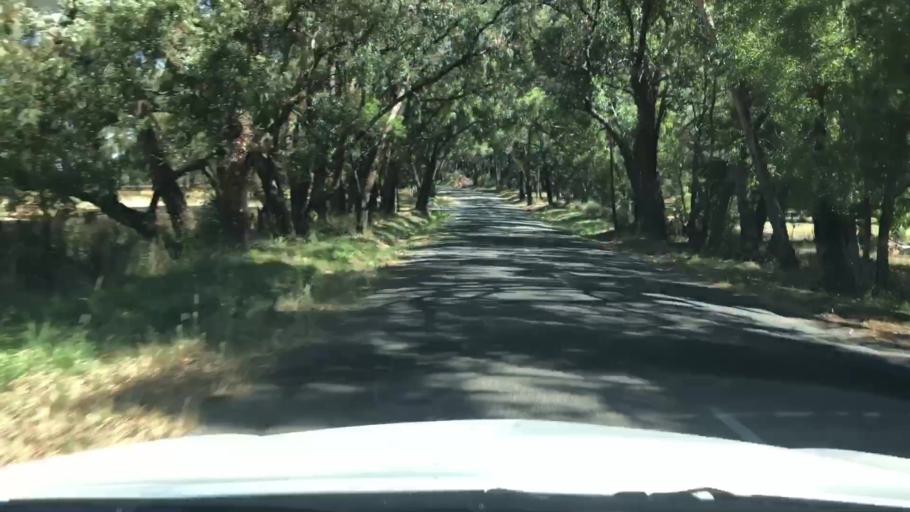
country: AU
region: Victoria
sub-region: Yarra Ranges
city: Macclesfield
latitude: -37.8755
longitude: 145.4782
